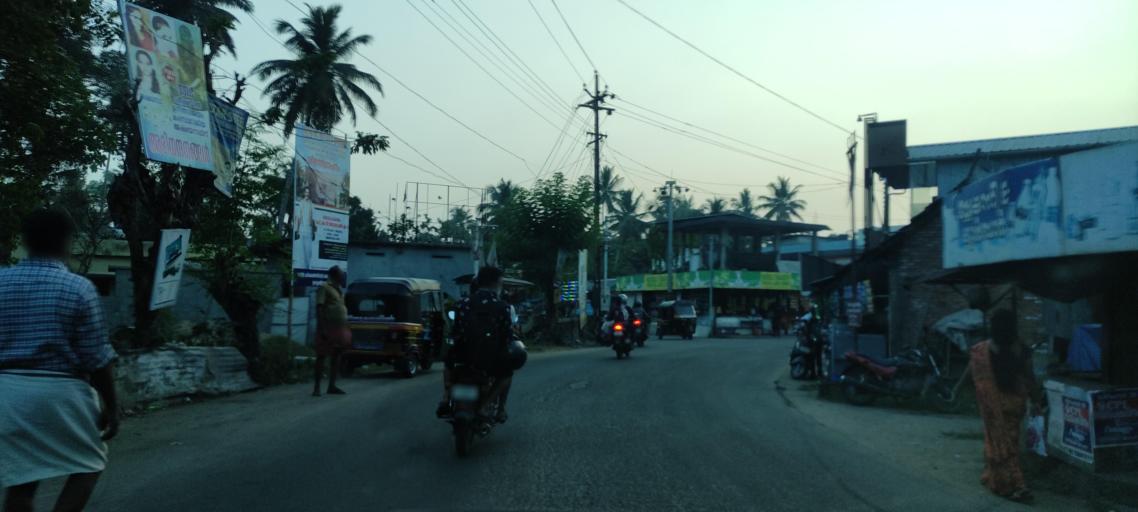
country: IN
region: Kerala
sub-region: Alappuzha
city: Kayankulam
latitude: 9.1255
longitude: 76.5019
